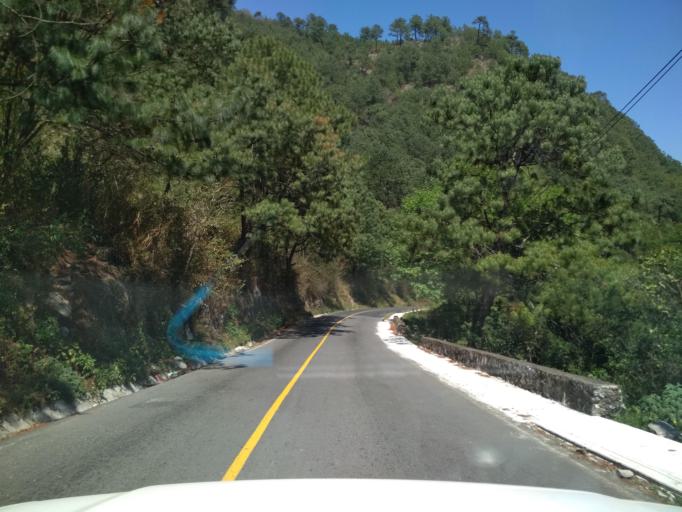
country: MX
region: Veracruz
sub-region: Tlilapan
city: Tonalixco
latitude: 18.7672
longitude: -97.0811
